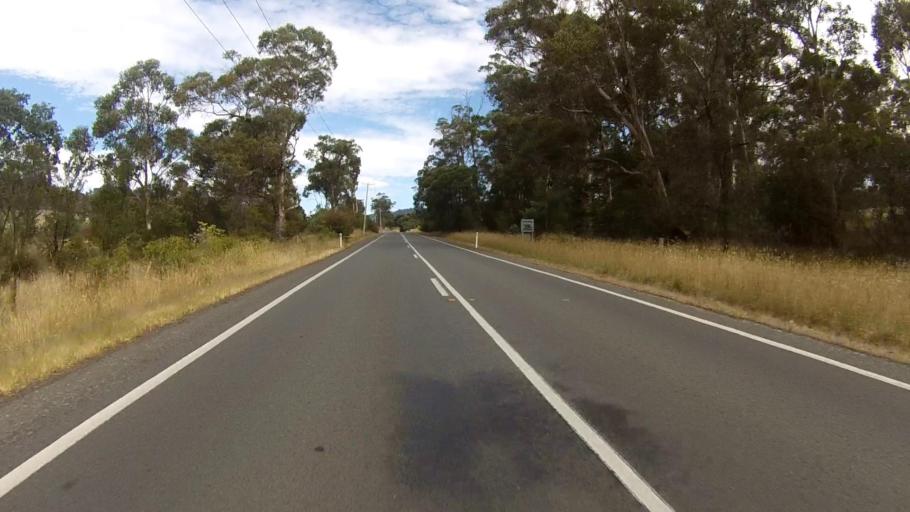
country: AU
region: Tasmania
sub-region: Clarence
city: Cambridge
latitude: -42.6768
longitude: 147.4048
